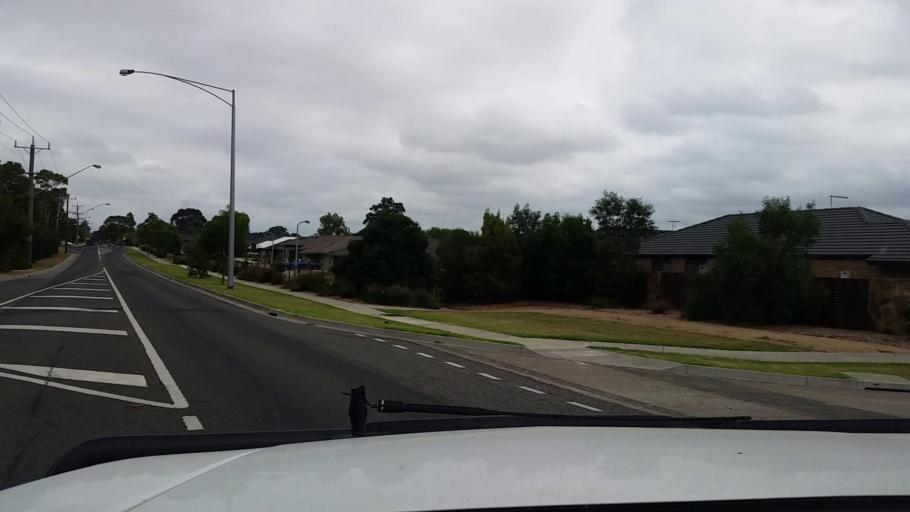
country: AU
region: Victoria
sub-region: Mornington Peninsula
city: Hastings
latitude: -38.2999
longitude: 145.1801
